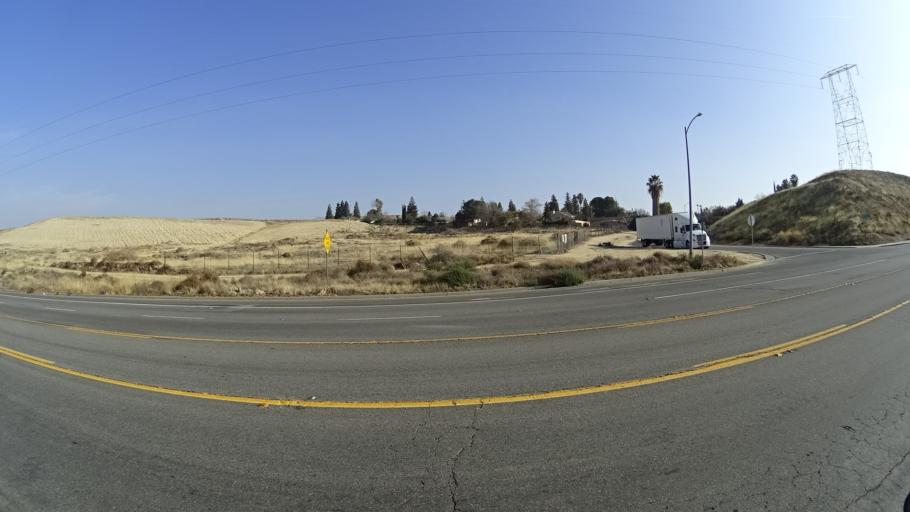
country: US
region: California
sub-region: Kern County
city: Oildale
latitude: 35.4099
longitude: -118.9341
